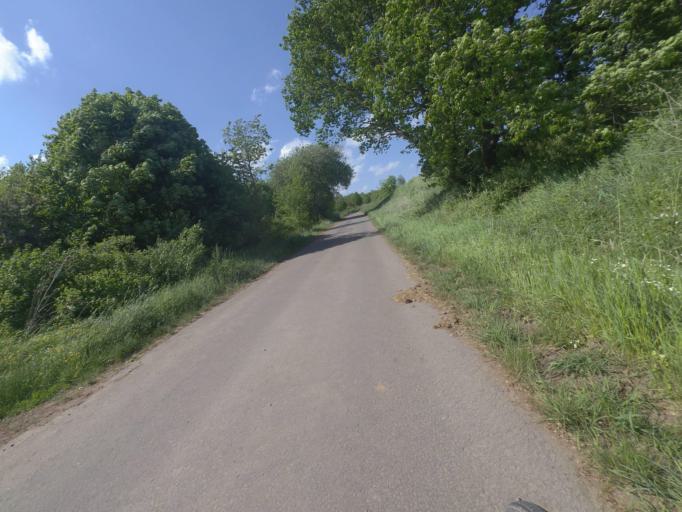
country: DE
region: Rheinland-Pfalz
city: Oberwiesen
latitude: 49.6843
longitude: 7.9665
